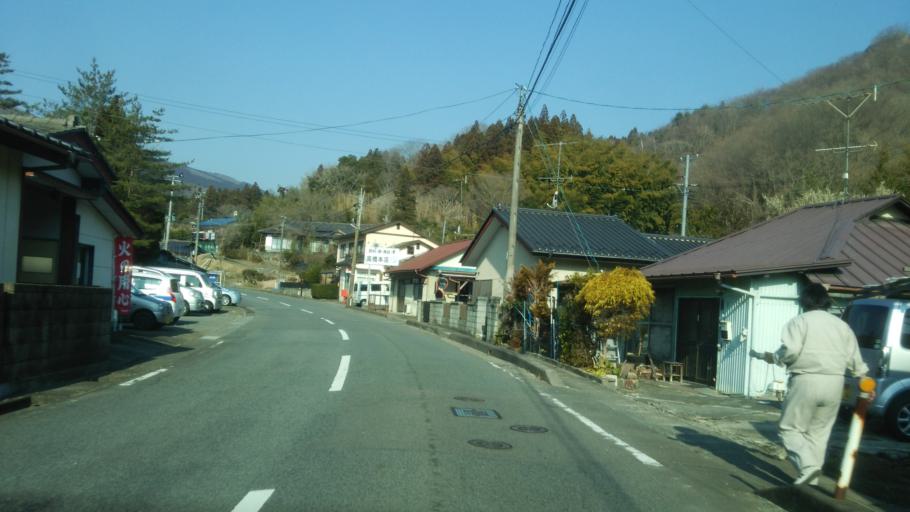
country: JP
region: Fukushima
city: Iwaki
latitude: 37.0288
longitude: 140.8204
